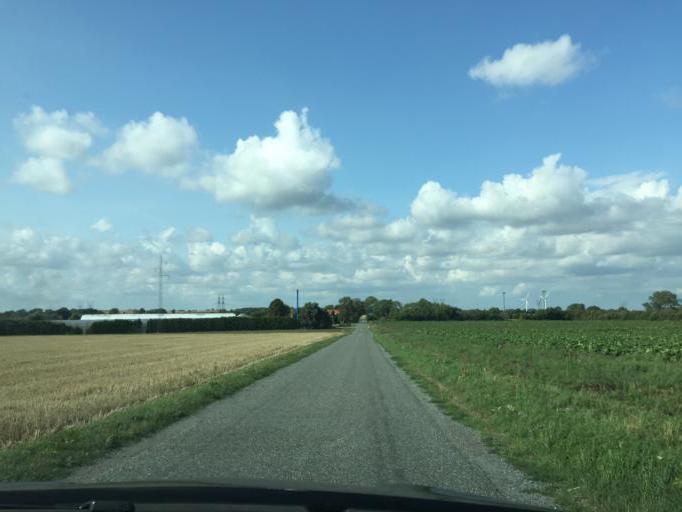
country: DK
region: South Denmark
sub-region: Odense Kommune
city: Bellinge
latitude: 55.3156
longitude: 10.3768
